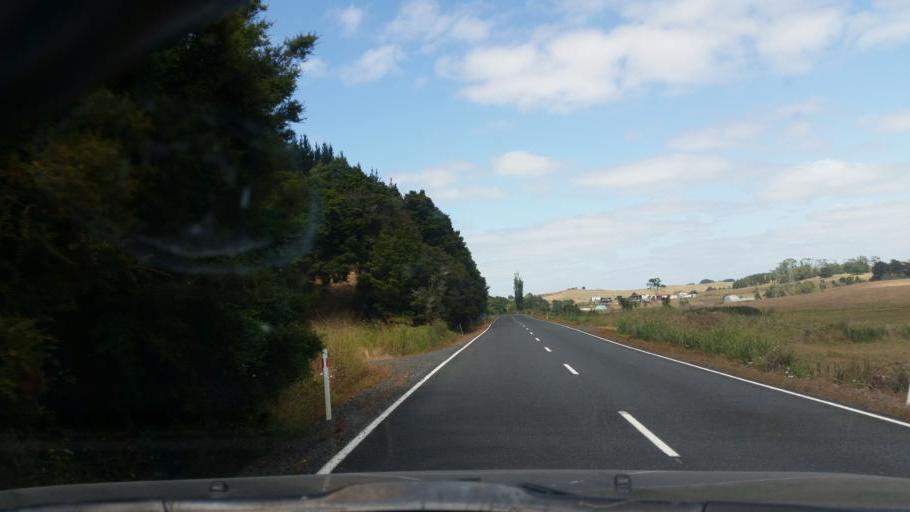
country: NZ
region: Northland
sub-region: Whangarei
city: Ruakaka
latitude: -35.9695
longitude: 174.2898
